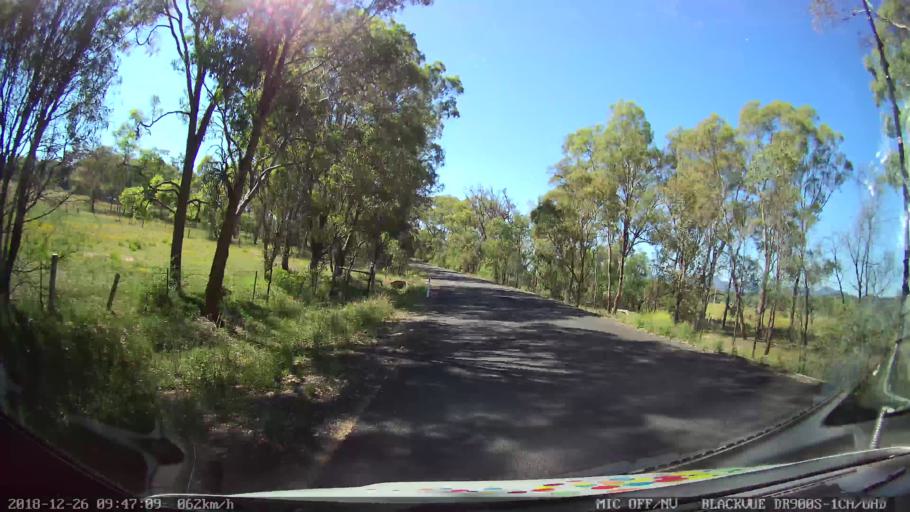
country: AU
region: New South Wales
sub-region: Mid-Western Regional
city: Kandos
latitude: -32.9768
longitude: 150.1045
